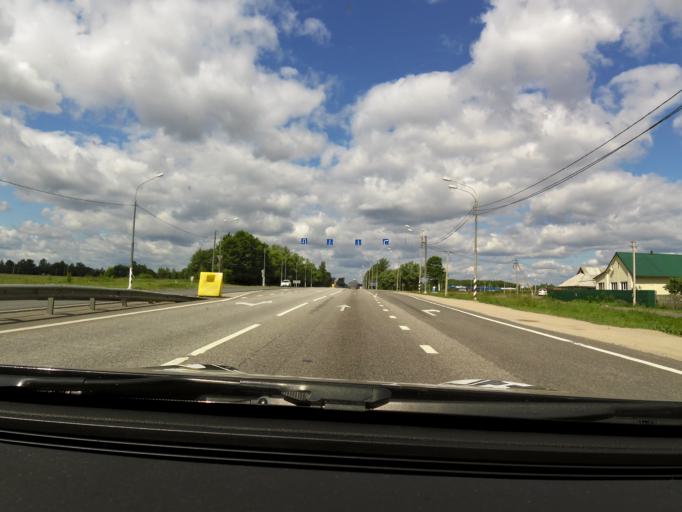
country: RU
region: Tverskaya
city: Likhoslavl'
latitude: 56.9839
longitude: 35.2355
